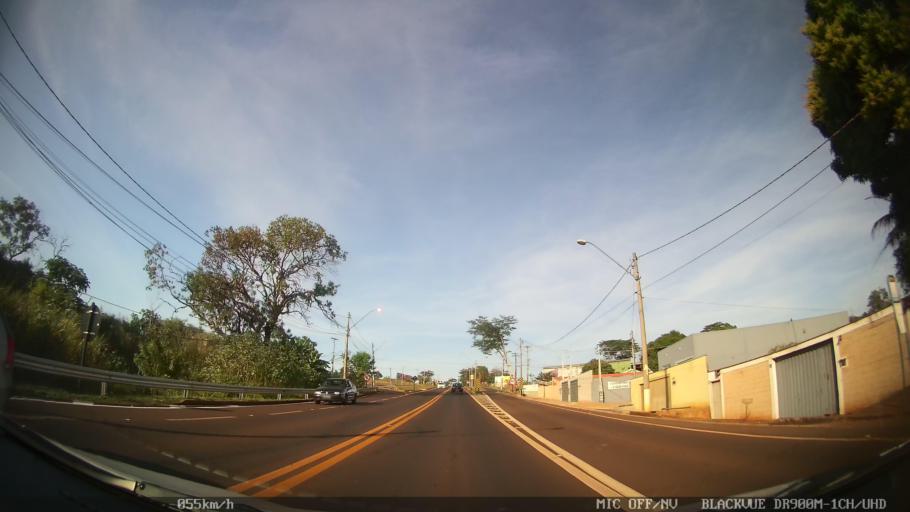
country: BR
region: Sao Paulo
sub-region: Ribeirao Preto
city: Ribeirao Preto
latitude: -21.2696
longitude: -47.8173
